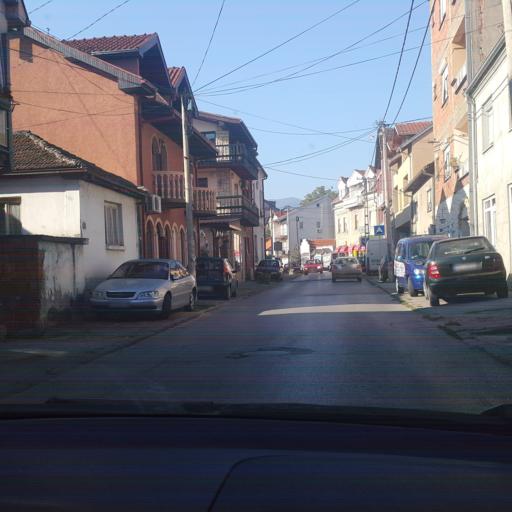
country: RS
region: Central Serbia
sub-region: Toplicki Okrug
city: Prokuplje
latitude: 43.2338
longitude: 21.5849
